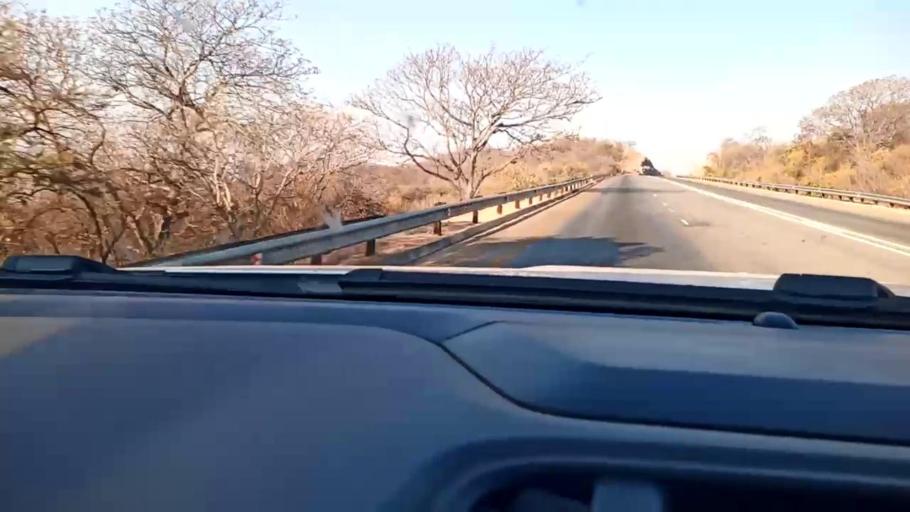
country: ZA
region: Limpopo
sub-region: Mopani District Municipality
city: Duiwelskloof
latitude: -23.6368
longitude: 30.1460
